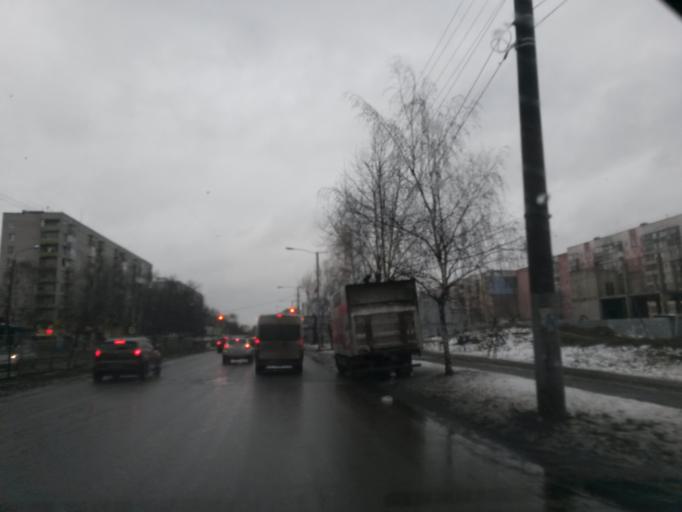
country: RU
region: Jaroslavl
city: Yaroslavl
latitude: 57.6473
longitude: 39.9529
